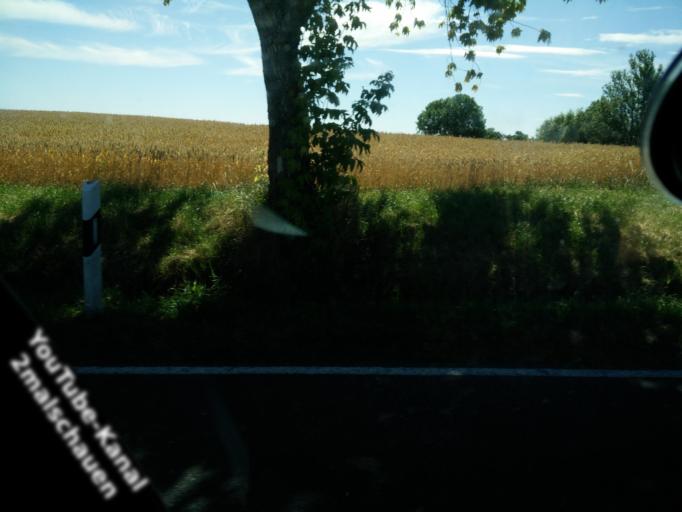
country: DE
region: Saxony
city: Waldheim
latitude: 51.0931
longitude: 13.0474
